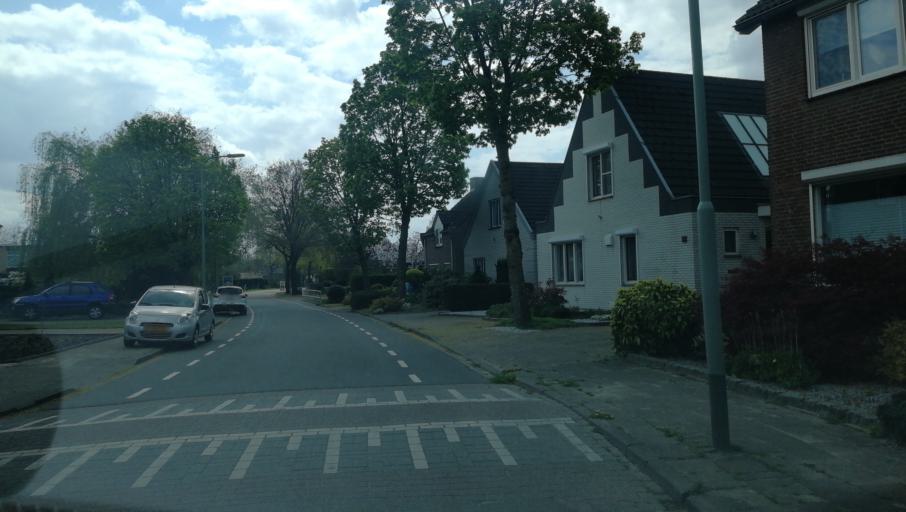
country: NL
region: Limburg
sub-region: Gemeente Venray
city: Venray
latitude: 51.4538
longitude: 6.0244
